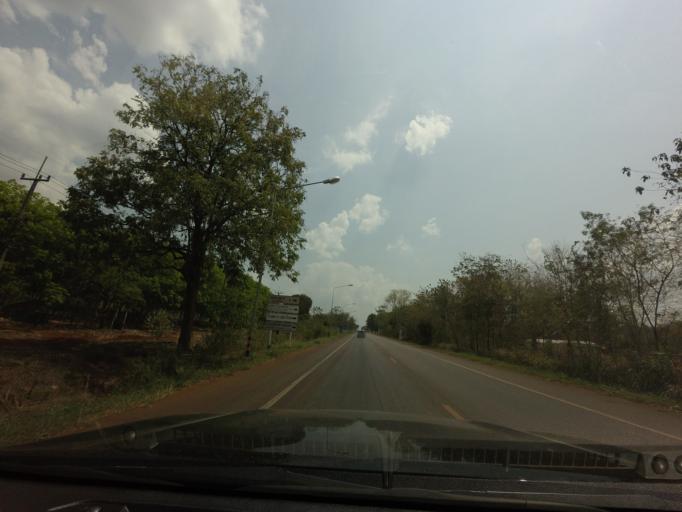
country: TH
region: Kanchanaburi
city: Sai Yok
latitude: 14.1327
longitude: 99.1588
